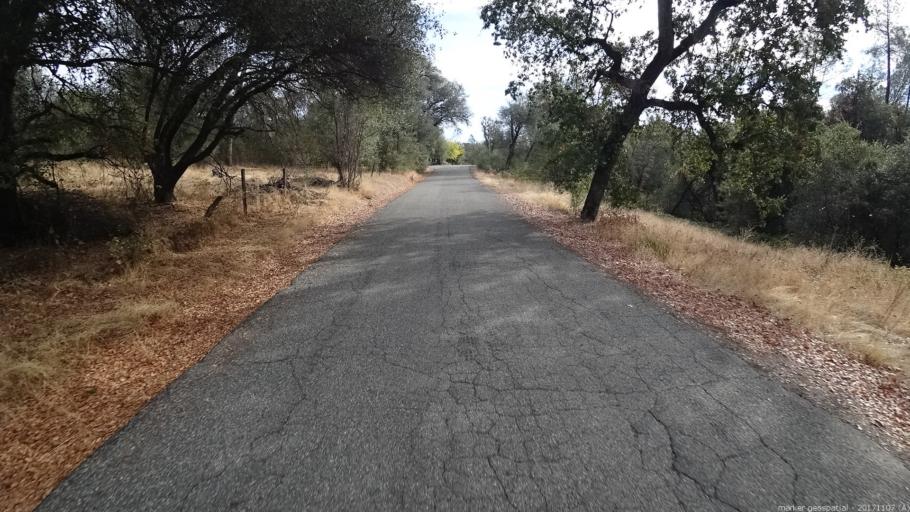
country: US
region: California
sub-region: Shasta County
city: Shasta
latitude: 40.5024
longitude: -122.5771
